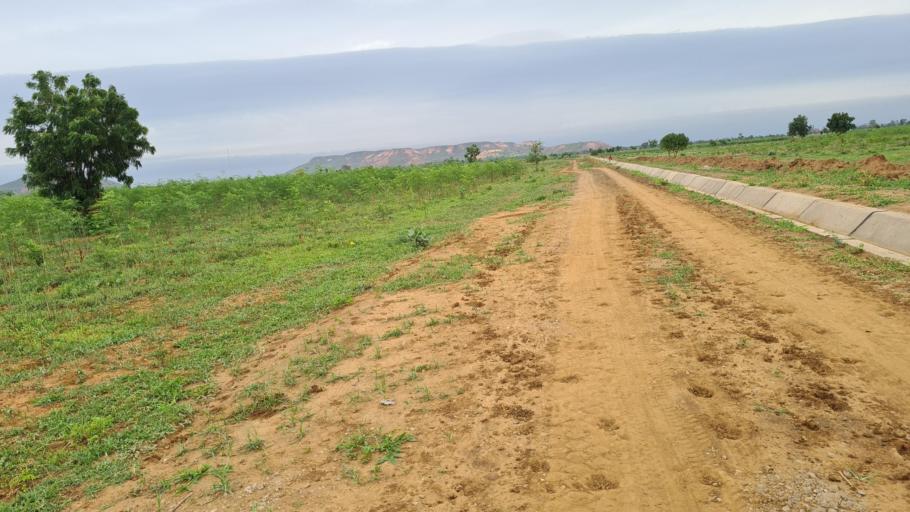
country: NE
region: Tahoua
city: Birni N Konni
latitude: 13.8355
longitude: 5.2676
